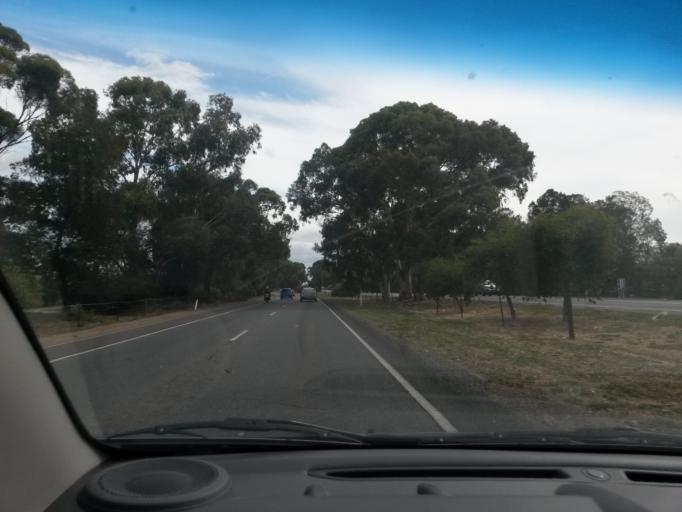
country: AU
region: South Australia
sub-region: Salisbury
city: Salisbury
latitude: -34.7863
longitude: 138.6516
